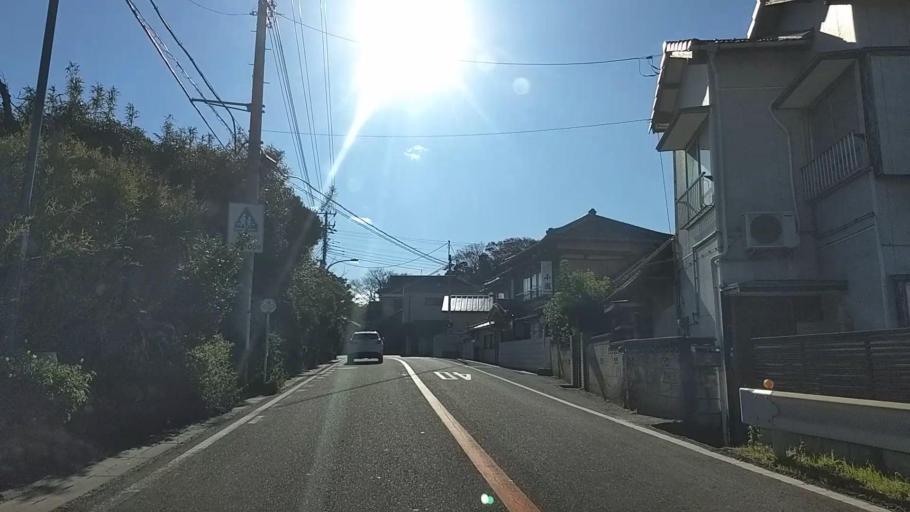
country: JP
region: Chiba
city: Futtsu
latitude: 35.1477
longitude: 139.8317
